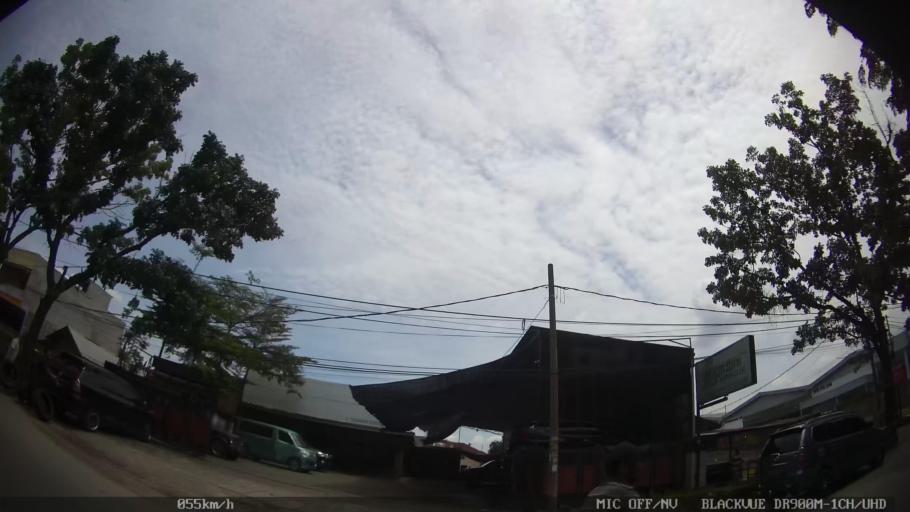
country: ID
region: North Sumatra
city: Sunggal
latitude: 3.5407
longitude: 98.6428
